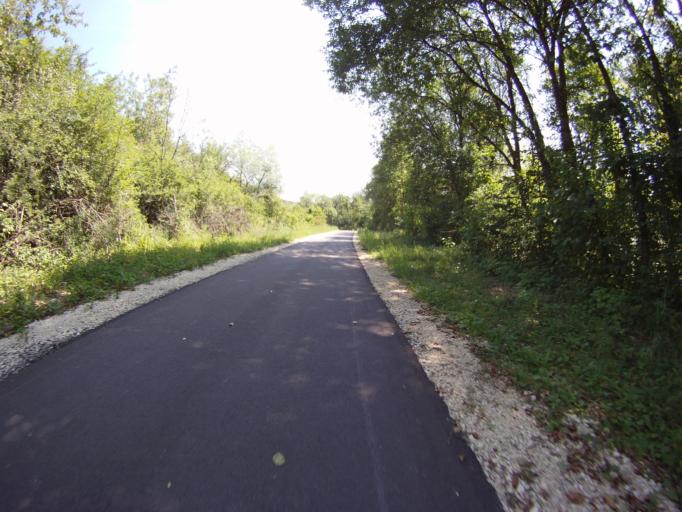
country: FR
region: Lorraine
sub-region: Departement de Meurthe-et-Moselle
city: Liverdun
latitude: 48.7580
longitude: 6.0486
